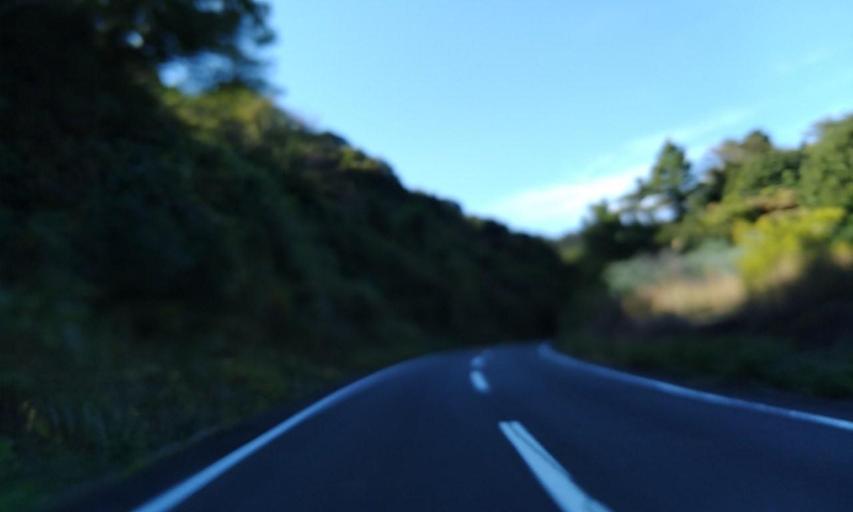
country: JP
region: Shizuoka
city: Hamakita
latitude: 34.8228
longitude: 137.6436
